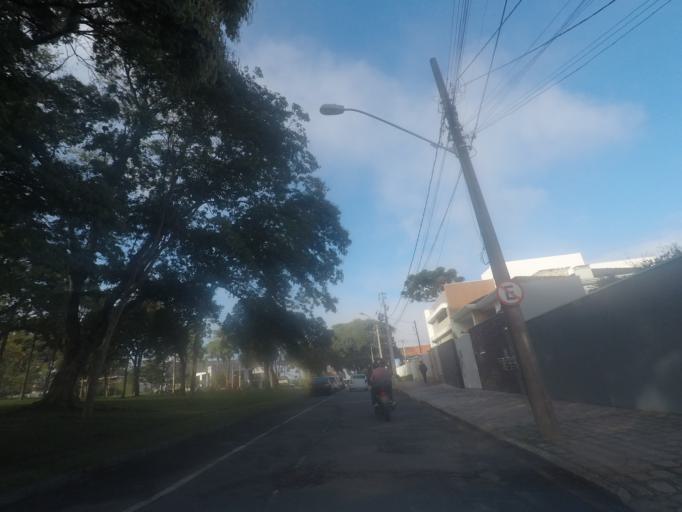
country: BR
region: Parana
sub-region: Curitiba
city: Curitiba
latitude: -25.4005
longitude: -49.2645
